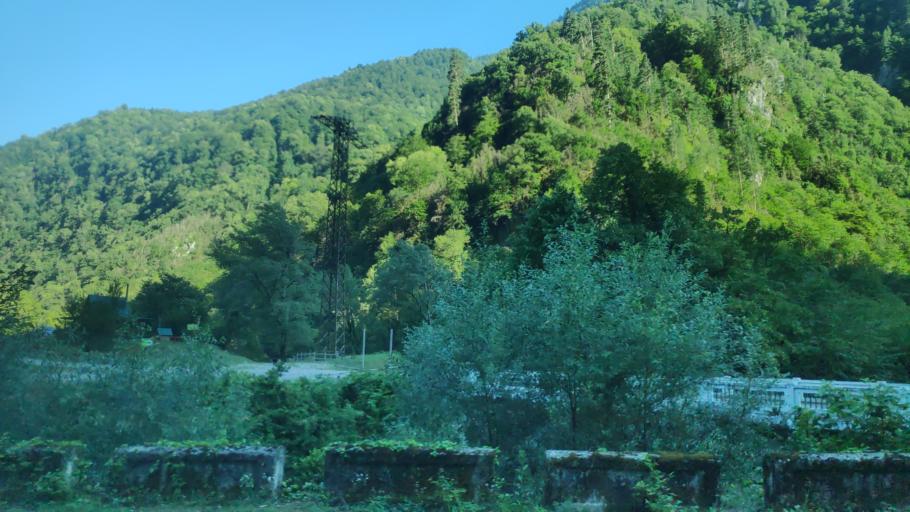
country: GE
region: Abkhazia
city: Gagra
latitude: 43.3692
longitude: 40.4583
